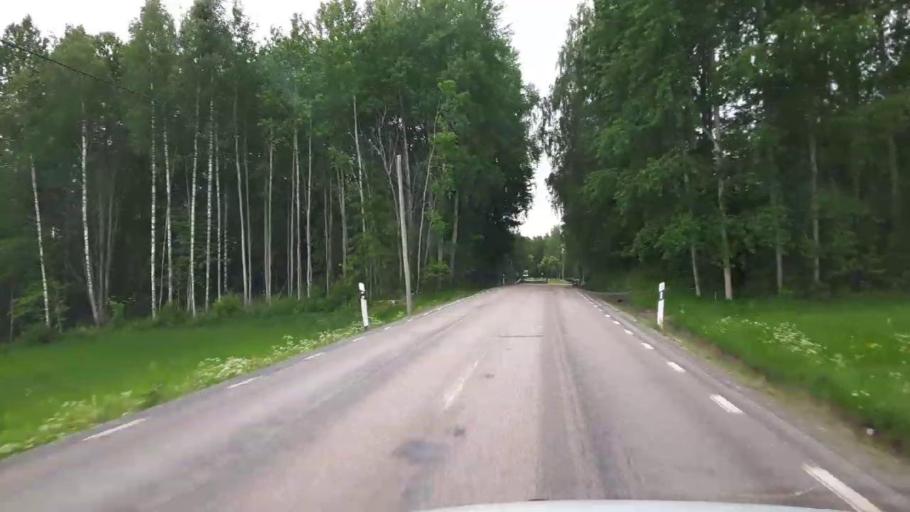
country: SE
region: Vaestmanland
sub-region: Kopings Kommun
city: Kolsva
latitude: 59.7061
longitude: 15.7948
